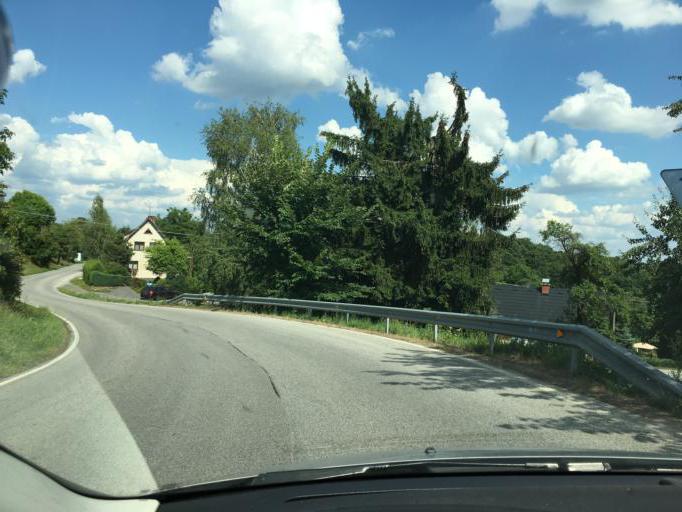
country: CZ
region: Liberecky
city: Zelezny Brod
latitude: 50.6116
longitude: 15.2738
